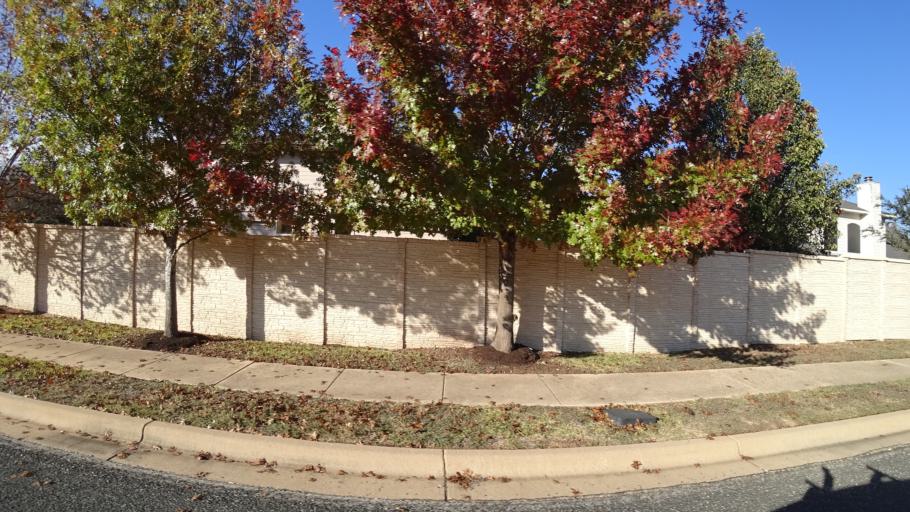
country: US
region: Texas
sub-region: Williamson County
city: Brushy Creek
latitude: 30.4958
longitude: -97.7455
